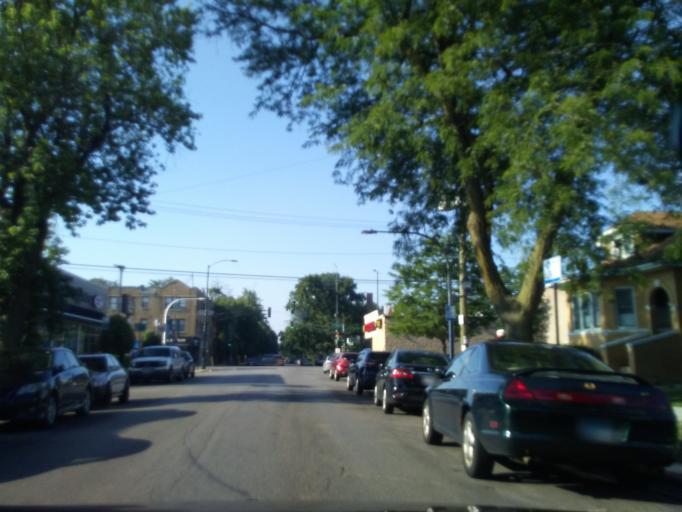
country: US
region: Illinois
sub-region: Cook County
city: Oak Park
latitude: 41.9323
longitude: -87.7368
